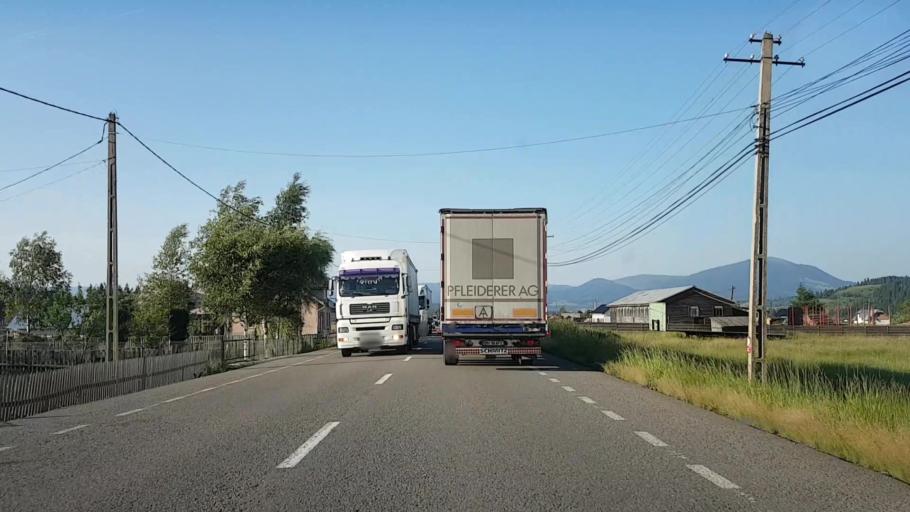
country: RO
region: Suceava
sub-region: Comuna Poiana Stampei
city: Poiana Stampei
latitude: 47.3107
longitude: 25.1283
